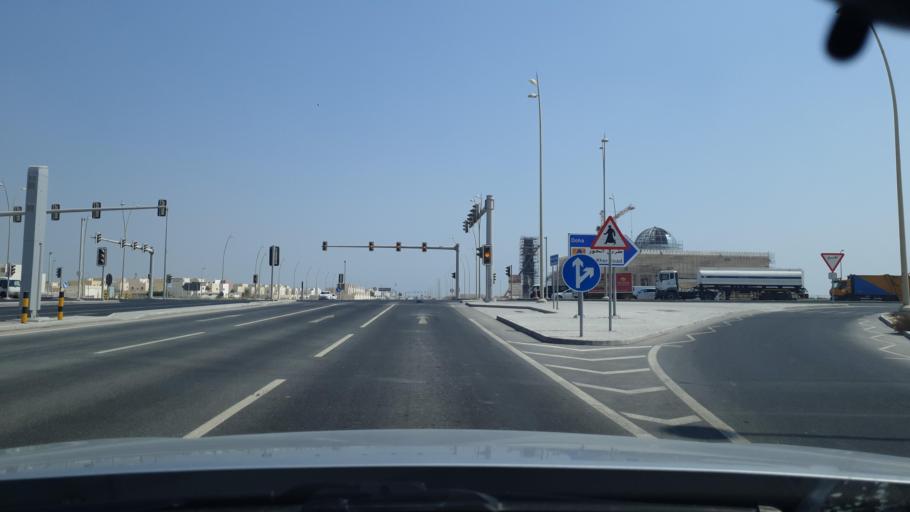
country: QA
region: Al Khawr
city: Al Khawr
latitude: 25.6633
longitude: 51.5002
